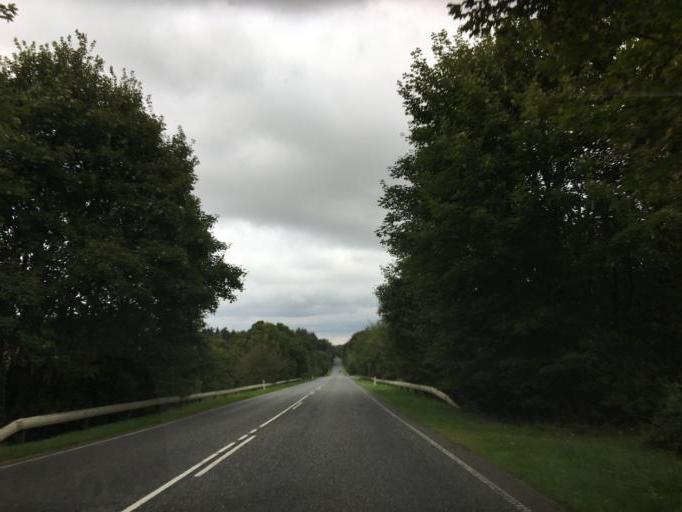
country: DK
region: South Denmark
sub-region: Kolding Kommune
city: Kolding
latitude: 55.5692
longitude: 9.4975
